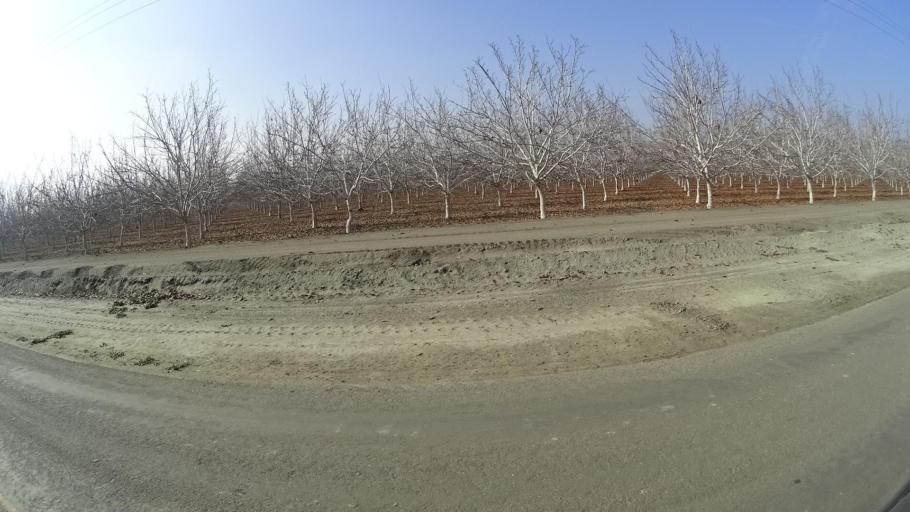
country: US
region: California
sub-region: Kern County
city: Buttonwillow
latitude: 35.3670
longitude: -119.4123
